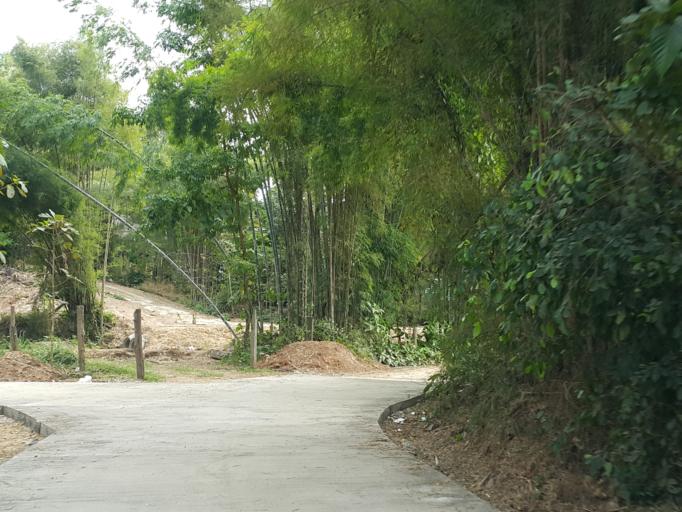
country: TH
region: Lampang
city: Hang Chat
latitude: 18.4695
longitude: 99.4179
